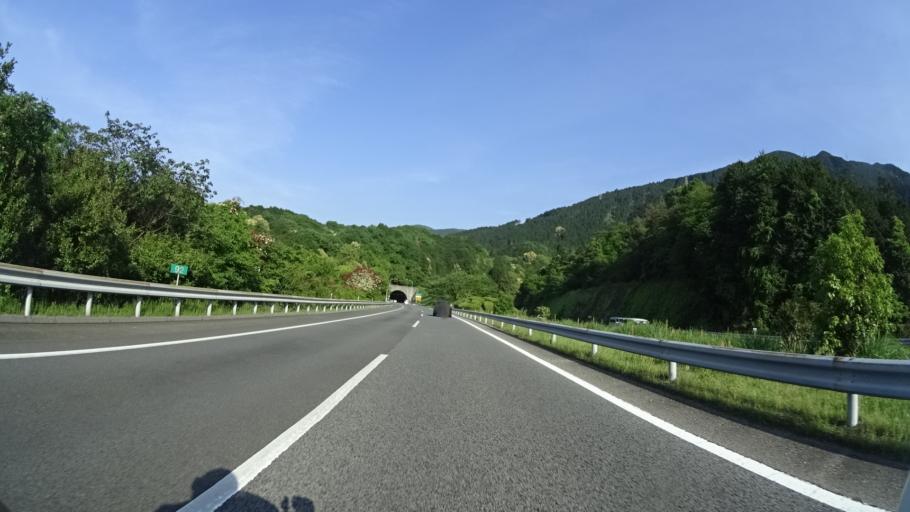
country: JP
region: Ehime
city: Saijo
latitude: 33.9097
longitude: 133.2500
